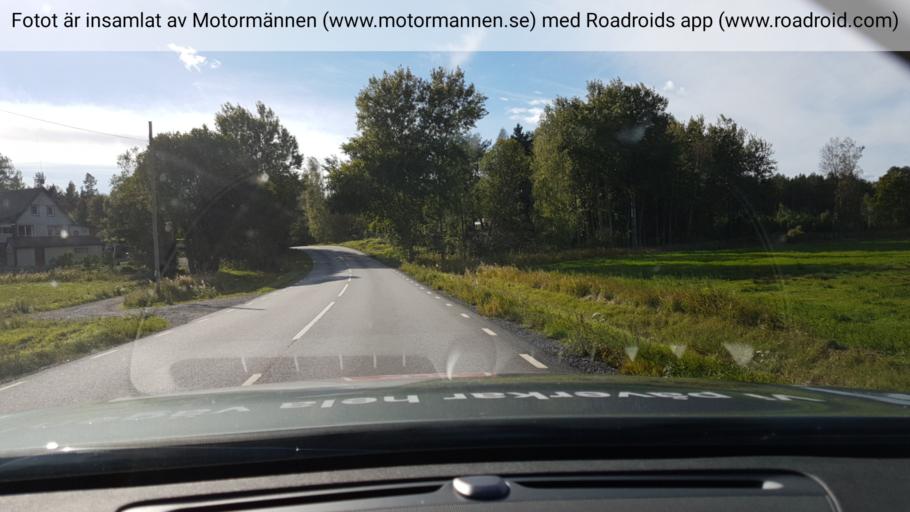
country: SE
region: OEstergoetland
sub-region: Valdemarsviks Kommun
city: Valdemarsvik
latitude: 58.1662
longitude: 16.5508
